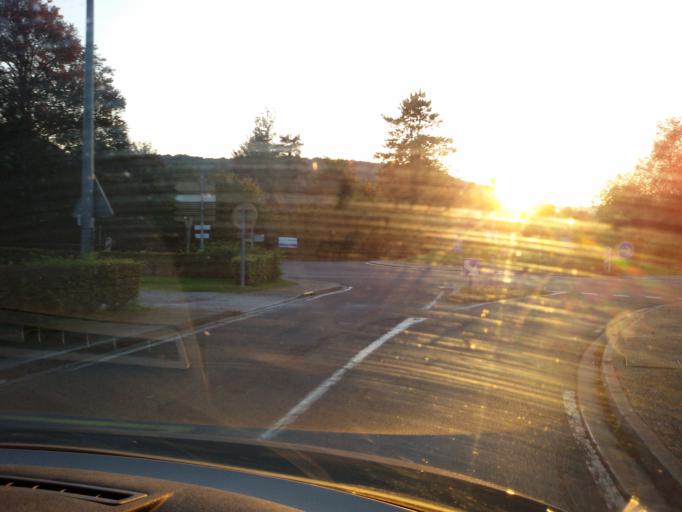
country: FR
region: Lower Normandy
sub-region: Departement du Calvados
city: Ablon
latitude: 49.4103
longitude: 0.3018
